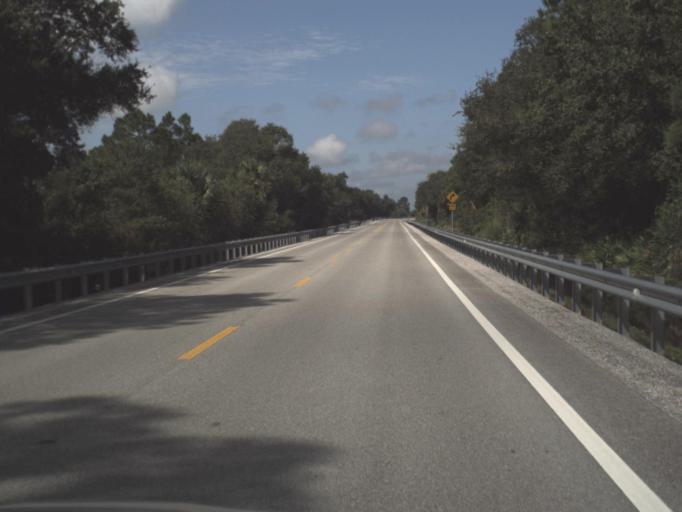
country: US
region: Florida
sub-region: Sarasota County
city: Warm Mineral Springs
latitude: 27.1957
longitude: -82.2180
